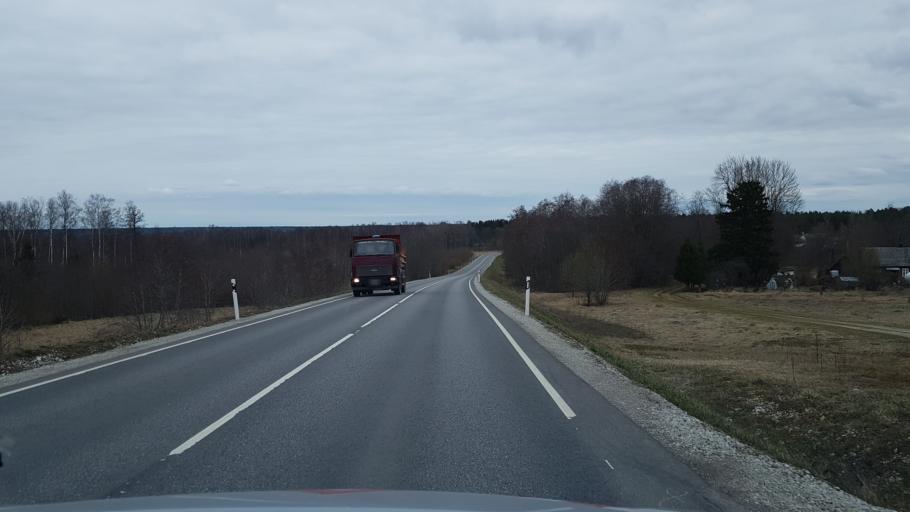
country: EE
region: Ida-Virumaa
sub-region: Narva-Joesuu linn
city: Narva-Joesuu
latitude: 59.4073
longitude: 28.0671
